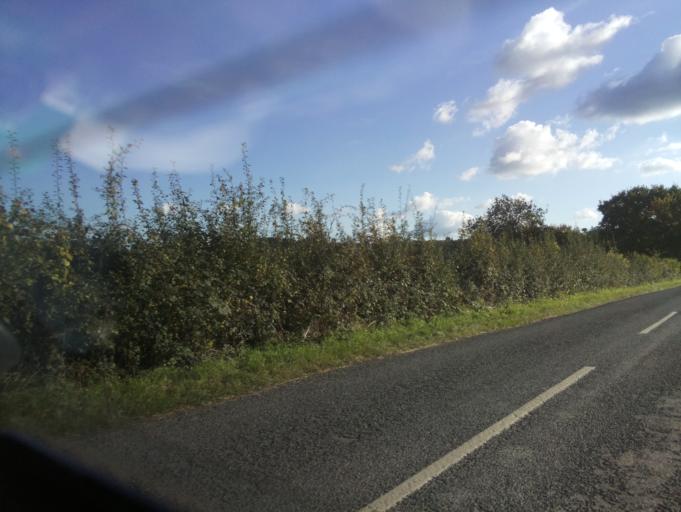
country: GB
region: England
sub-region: Herefordshire
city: Clifford
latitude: 52.1186
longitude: -3.0841
